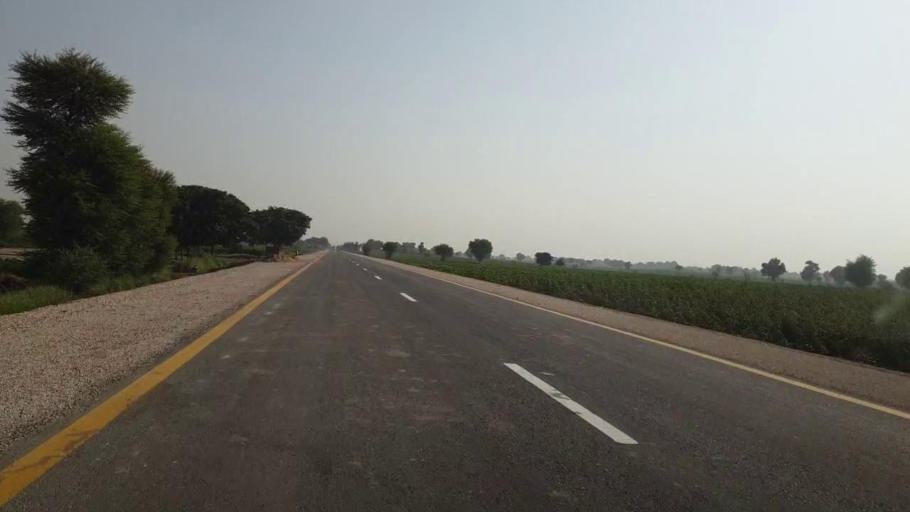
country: PK
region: Sindh
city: Bhan
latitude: 26.5420
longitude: 67.7874
